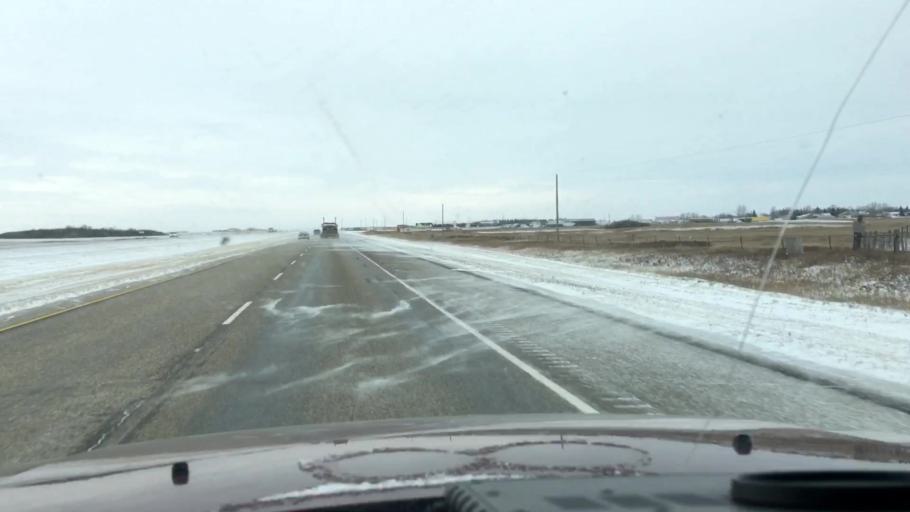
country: CA
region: Saskatchewan
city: Saskatoon
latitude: 51.6393
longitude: -106.4332
